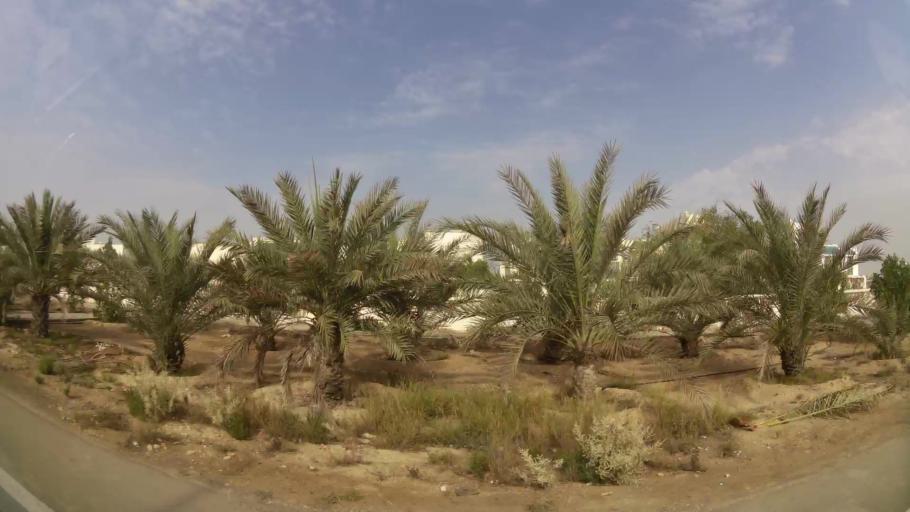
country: AE
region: Abu Dhabi
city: Abu Dhabi
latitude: 24.6597
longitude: 54.7591
